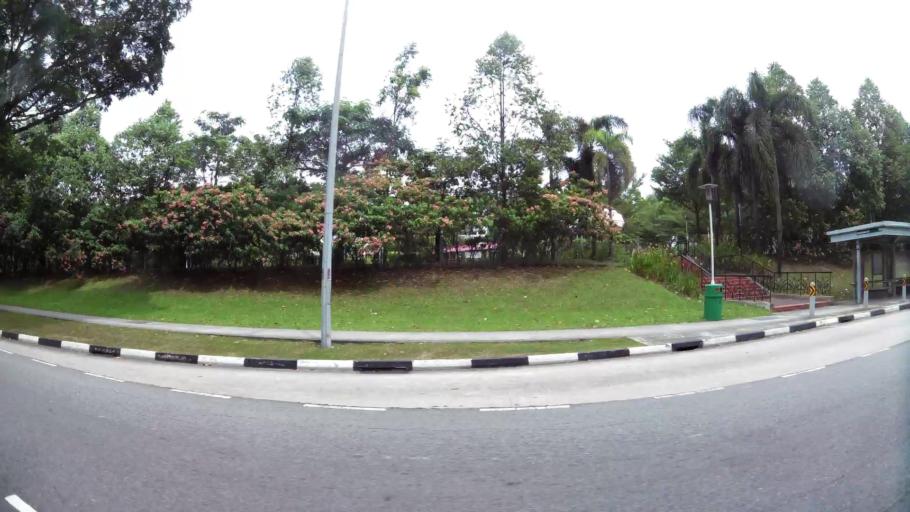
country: MY
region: Johor
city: Johor Bahru
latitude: 1.3368
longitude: 103.7180
